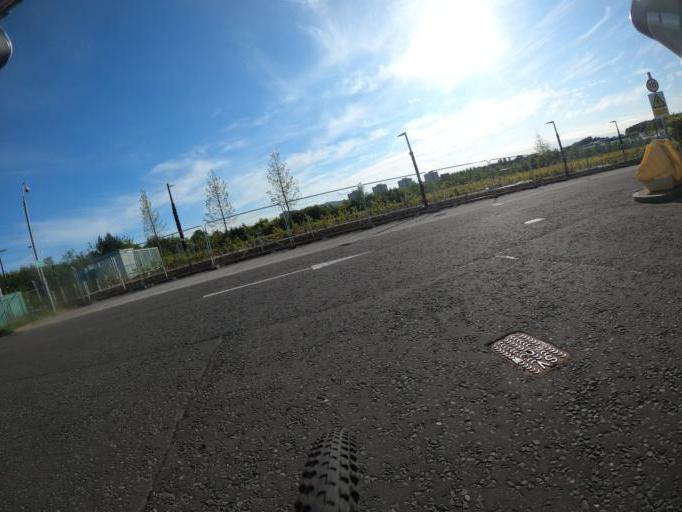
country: GB
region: Scotland
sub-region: Midlothian
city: Loanhead
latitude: 55.9191
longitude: -3.1288
